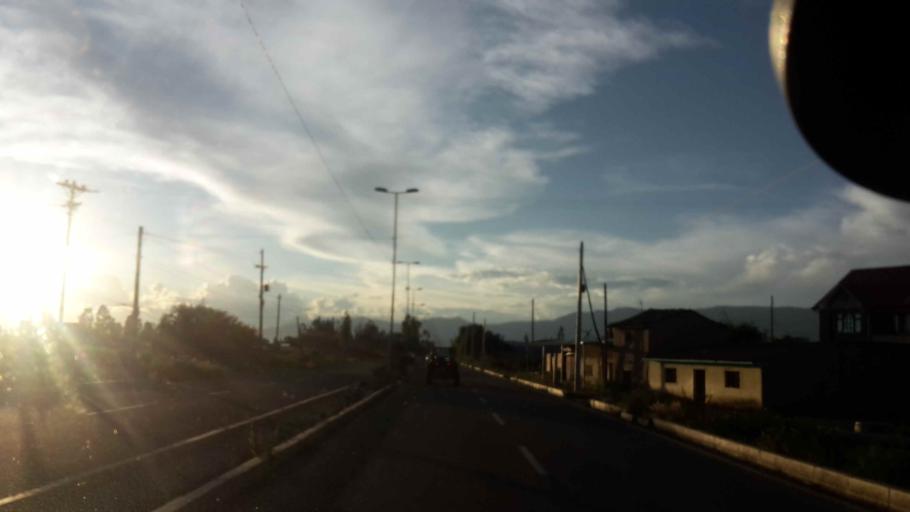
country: BO
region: Cochabamba
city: Arani
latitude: -17.5635
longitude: -65.7922
